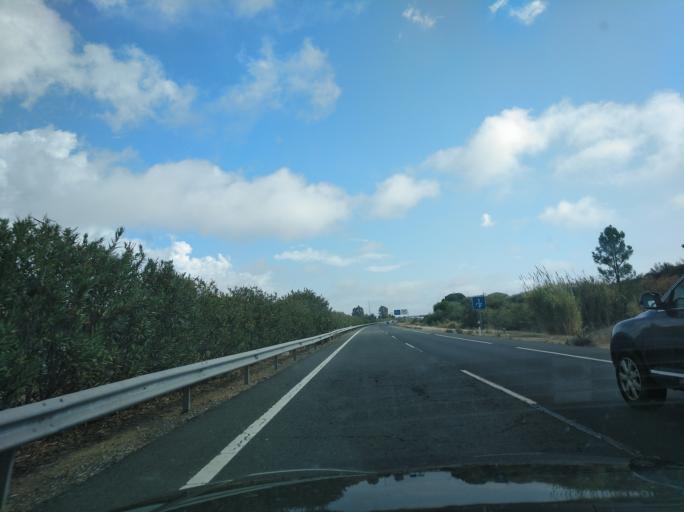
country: ES
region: Andalusia
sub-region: Provincia de Huelva
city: Aljaraque
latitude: 37.3229
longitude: -7.0816
